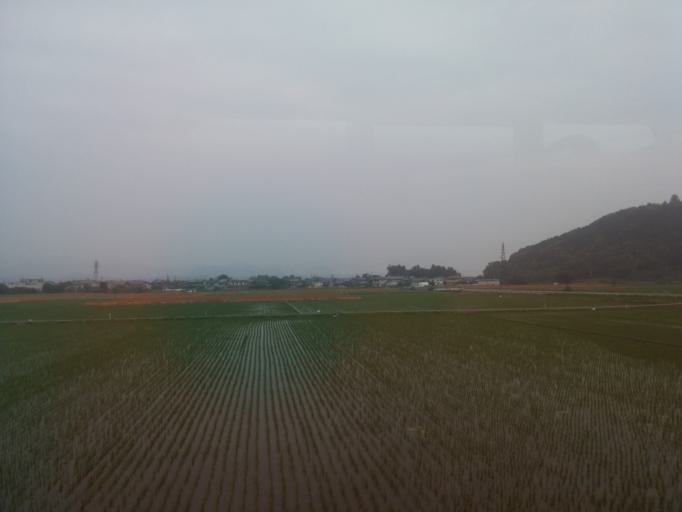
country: JP
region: Shiga Prefecture
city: Omihachiman
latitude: 35.1471
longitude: 136.1395
